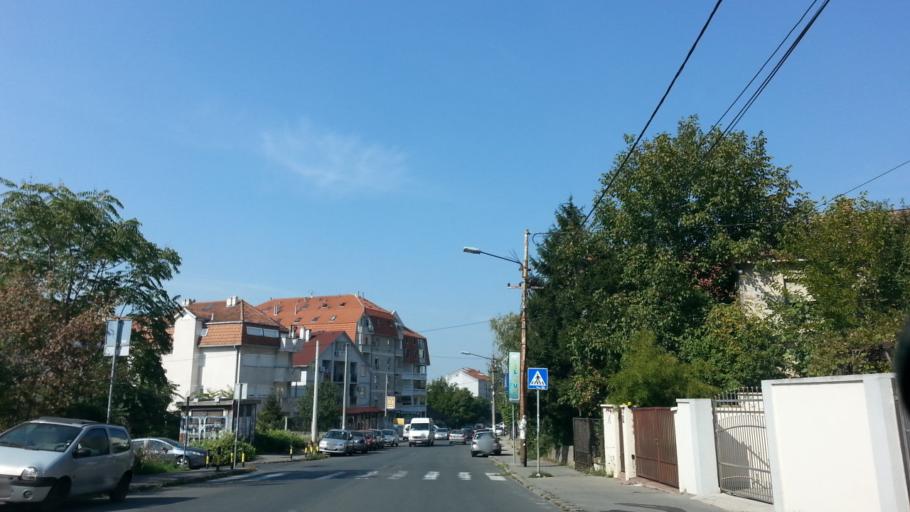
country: RS
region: Central Serbia
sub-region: Belgrade
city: Rakovica
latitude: 44.7542
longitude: 20.4235
